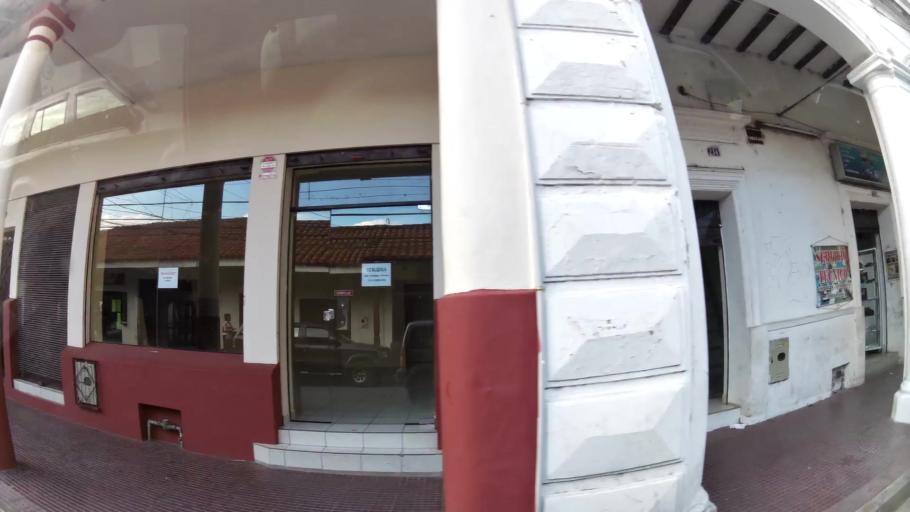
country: BO
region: Santa Cruz
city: Santa Cruz de la Sierra
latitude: -17.7819
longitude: -63.1844
